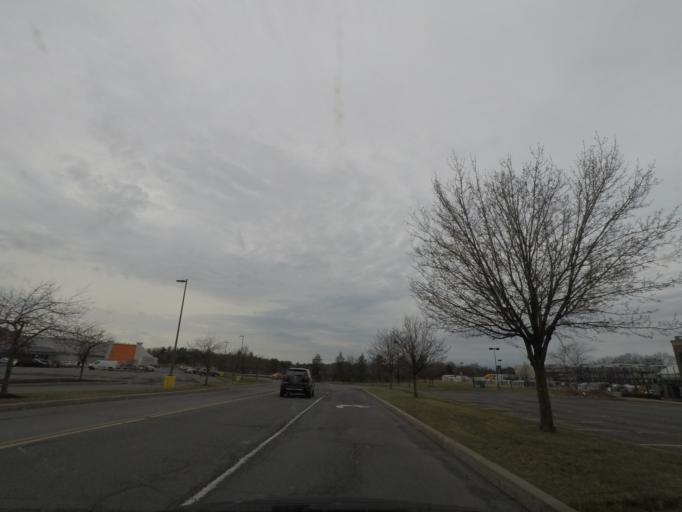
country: US
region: New York
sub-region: Albany County
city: Delmar
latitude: 42.6097
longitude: -73.7900
